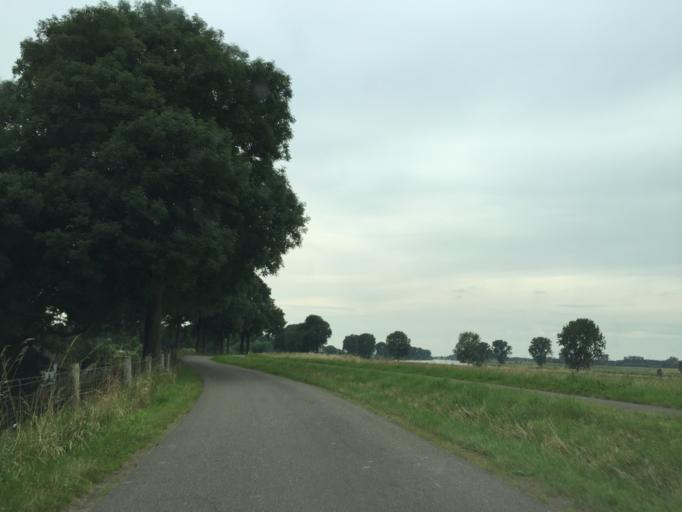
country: NL
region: Gelderland
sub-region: Gemeente Wijchen
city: Bergharen
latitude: 51.8165
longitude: 5.6284
